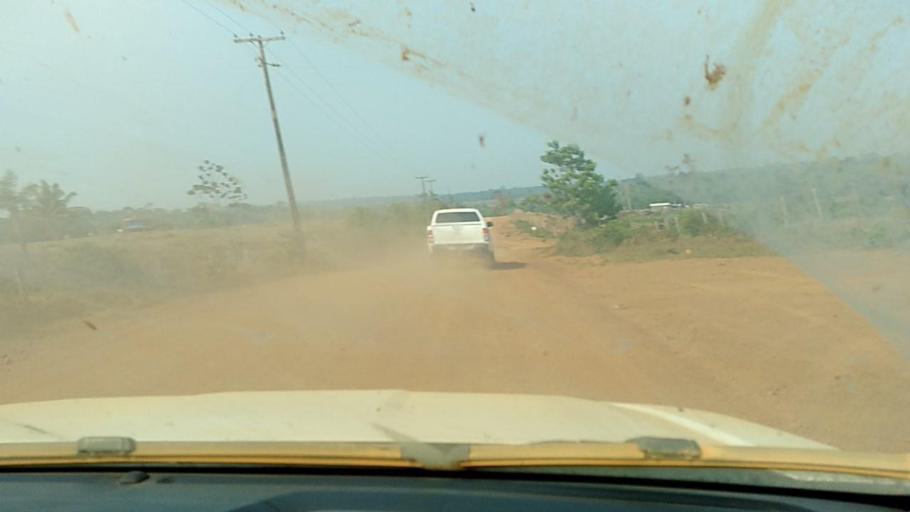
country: BR
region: Rondonia
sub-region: Porto Velho
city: Porto Velho
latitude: -8.8545
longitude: -64.1725
